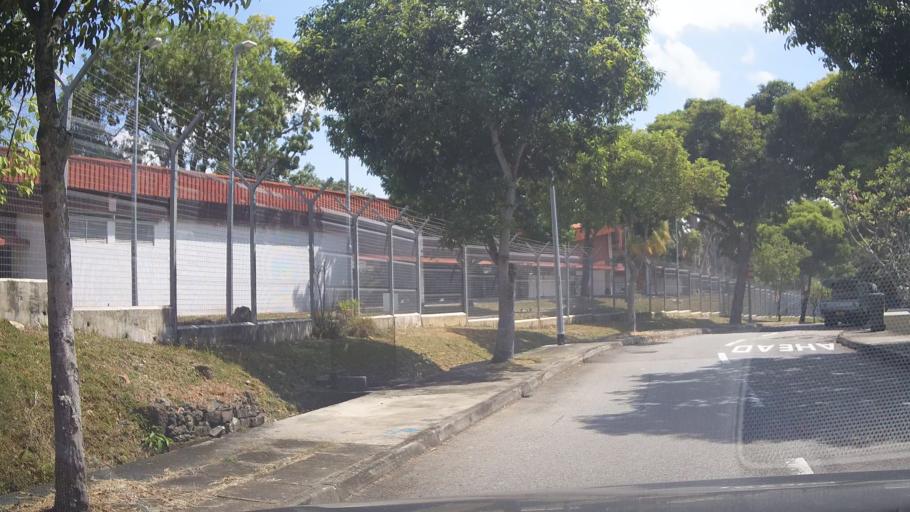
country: MY
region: Johor
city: Kampung Pasir Gudang Baru
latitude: 1.3663
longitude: 103.9739
